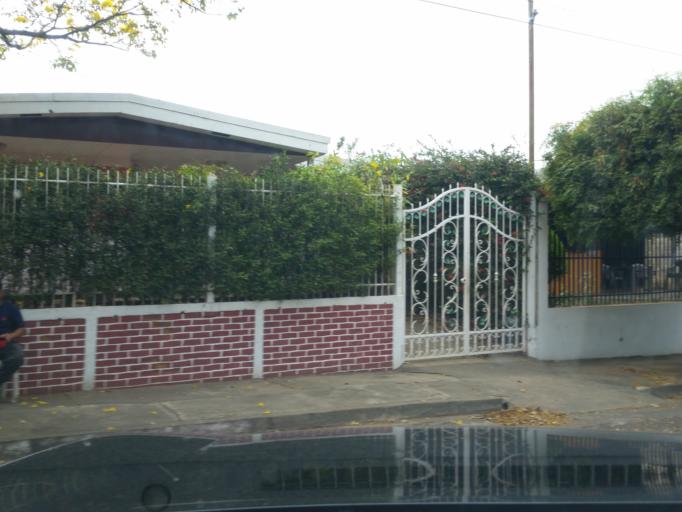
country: NI
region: Managua
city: Managua
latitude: 12.1176
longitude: -86.2539
